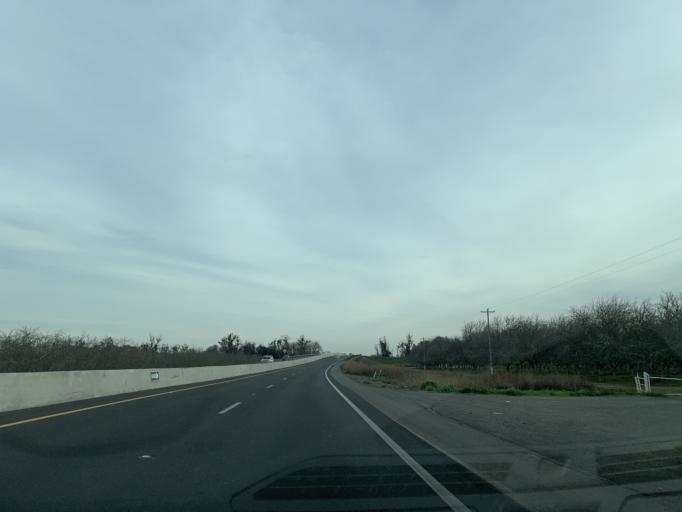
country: US
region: California
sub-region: Yuba County
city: Plumas Lake
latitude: 38.9089
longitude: -121.5949
